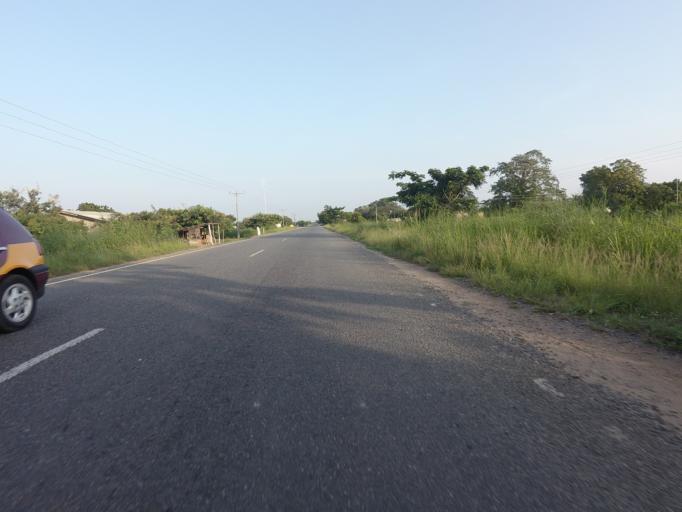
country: GH
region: Volta
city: Anloga
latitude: 5.9094
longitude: 0.7099
